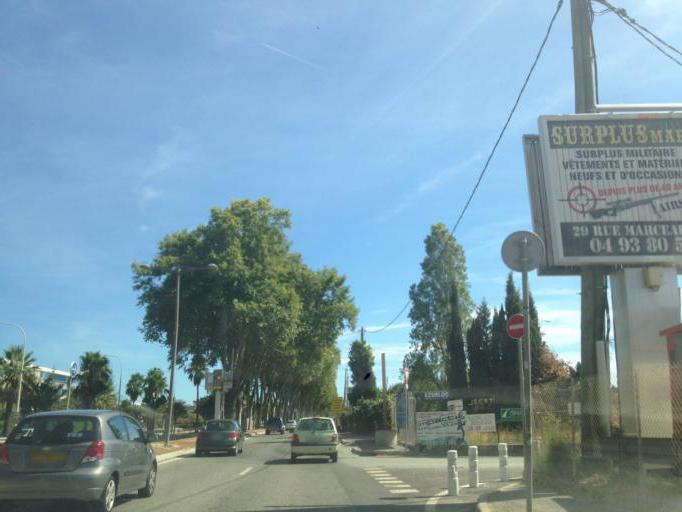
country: FR
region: Provence-Alpes-Cote d'Azur
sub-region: Departement des Alpes-Maritimes
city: Saint-Laurent-du-Var
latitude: 43.6864
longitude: 7.1973
